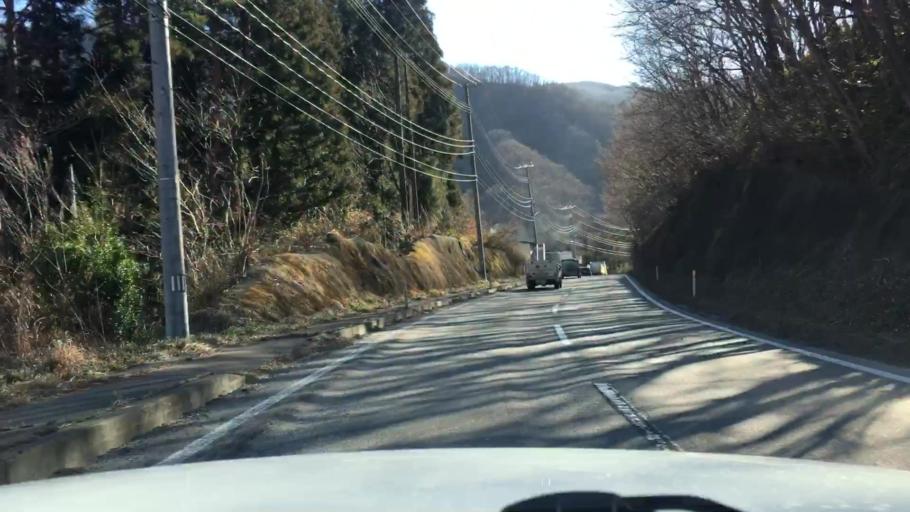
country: JP
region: Iwate
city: Miyako
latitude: 39.6223
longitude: 141.8109
